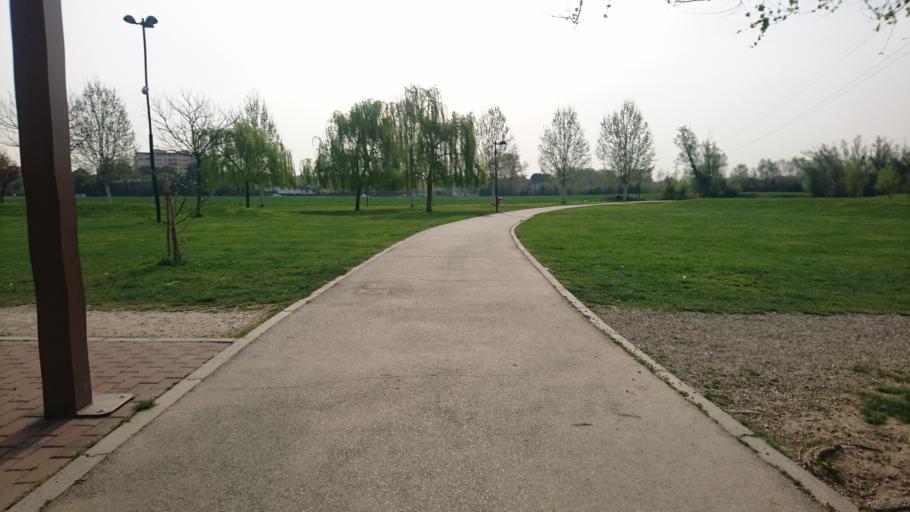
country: IT
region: Veneto
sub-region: Provincia di Padova
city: Mandriola-Sant'Agostino
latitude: 45.3778
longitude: 11.8627
